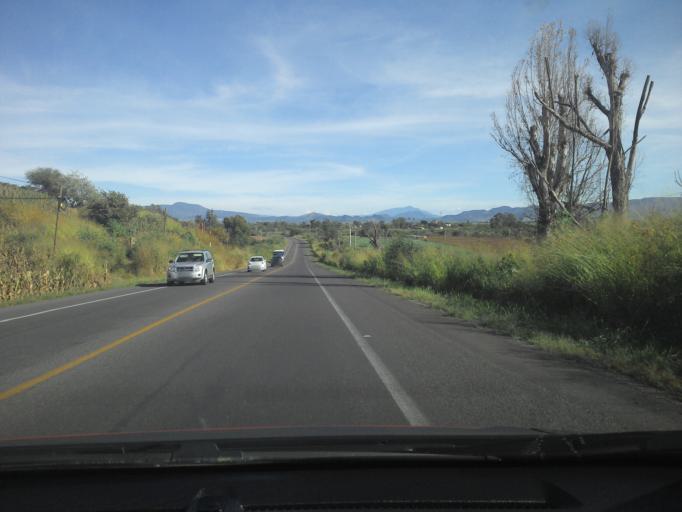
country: MX
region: Jalisco
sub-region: Teuchitlan
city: La Estanzuela
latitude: 20.6769
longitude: -103.8355
